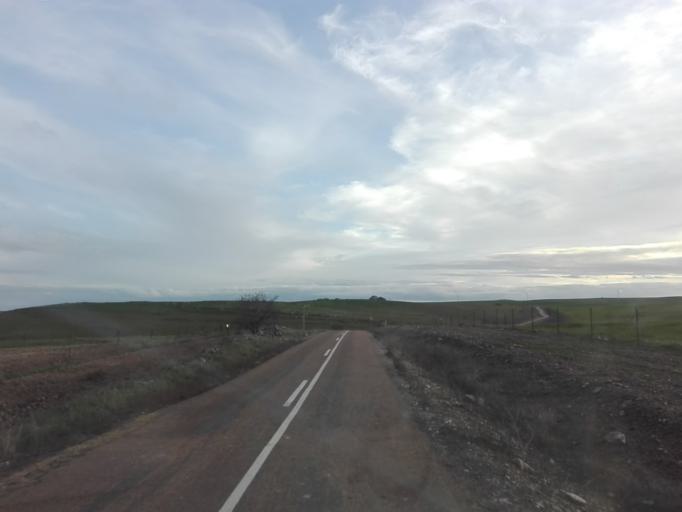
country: ES
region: Extremadura
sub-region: Provincia de Badajoz
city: Hinojosa del Valle
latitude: 38.4170
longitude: -6.1744
